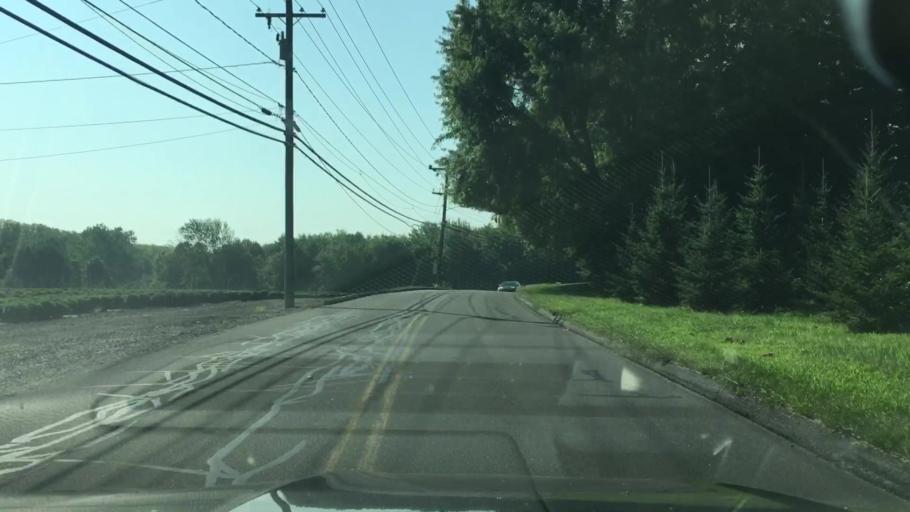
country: US
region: Connecticut
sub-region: New Haven County
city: Cheshire Village
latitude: 41.5475
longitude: -72.9040
